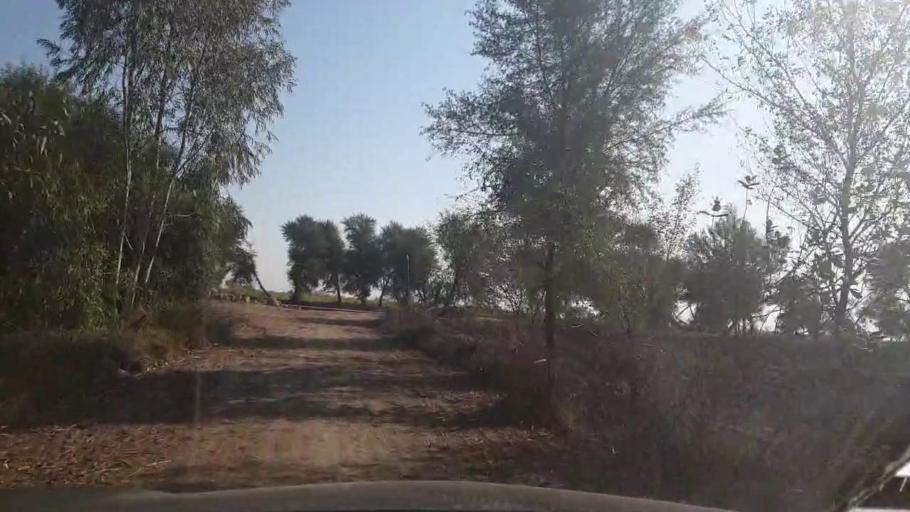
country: PK
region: Sindh
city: Khairpur
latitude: 28.1338
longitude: 69.6076
